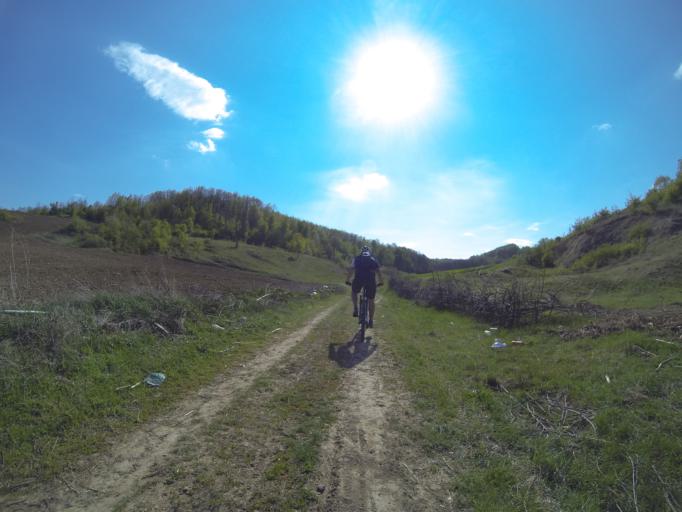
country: RO
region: Gorj
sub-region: Comuna Crusetu
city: Crusetu
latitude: 44.6249
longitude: 23.6315
